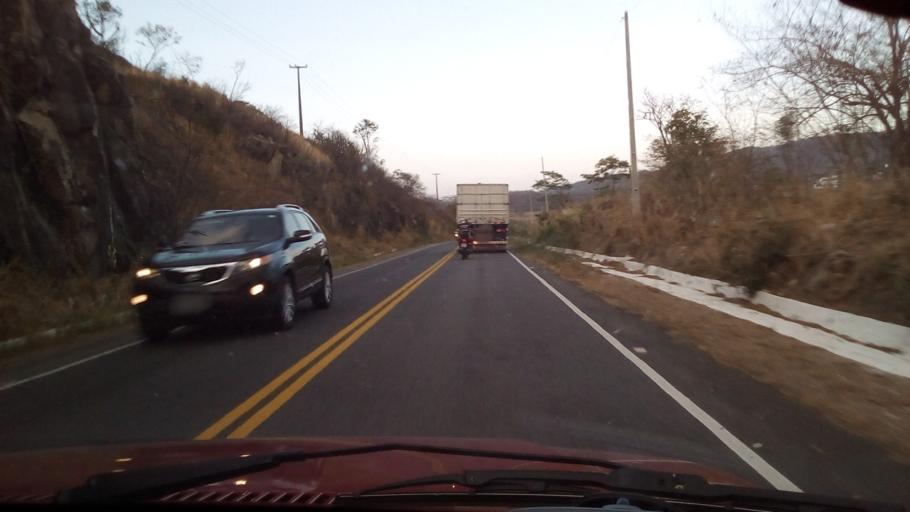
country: BR
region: Paraiba
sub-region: Bananeiras
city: Solanea
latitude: -6.7264
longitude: -35.5530
